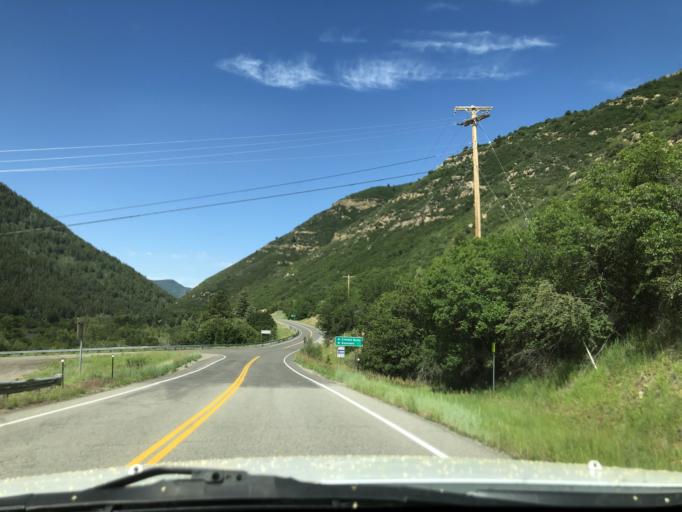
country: US
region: Colorado
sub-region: Delta County
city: Paonia
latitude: 38.9415
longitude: -107.3616
